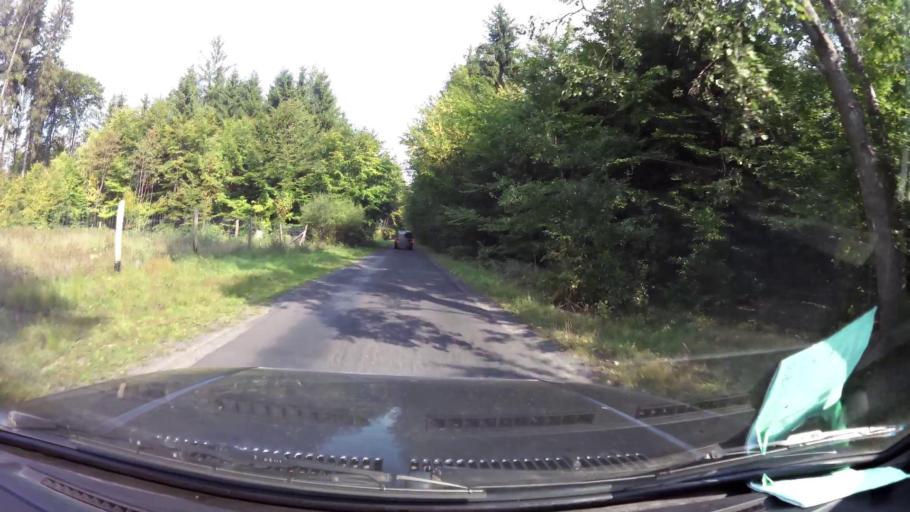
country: PL
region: West Pomeranian Voivodeship
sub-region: Powiat koszalinski
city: Bobolice
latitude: 54.0977
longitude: 16.4908
